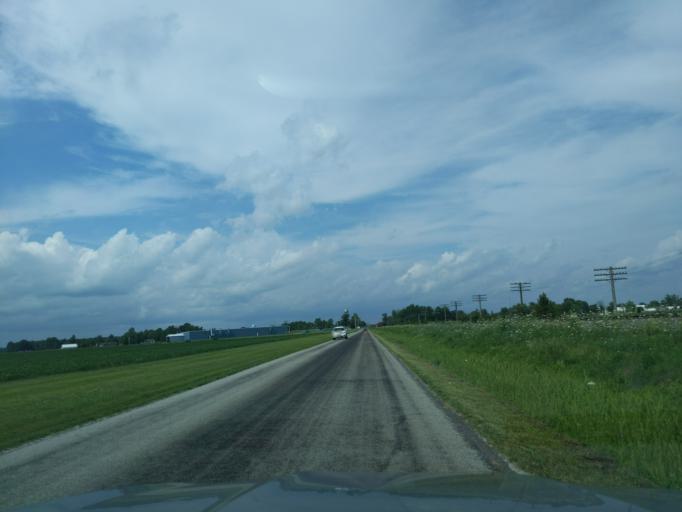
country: US
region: Indiana
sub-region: Ripley County
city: Osgood
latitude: 39.1193
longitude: -85.3026
